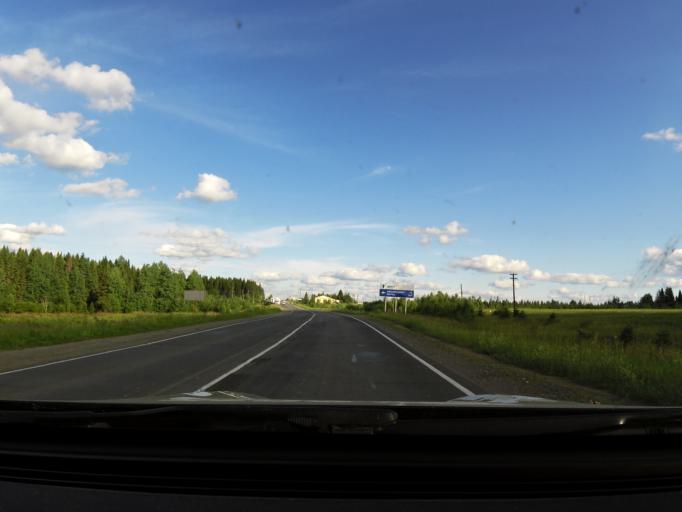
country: RU
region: Kirov
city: Omutninsk
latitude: 58.6862
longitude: 52.1380
